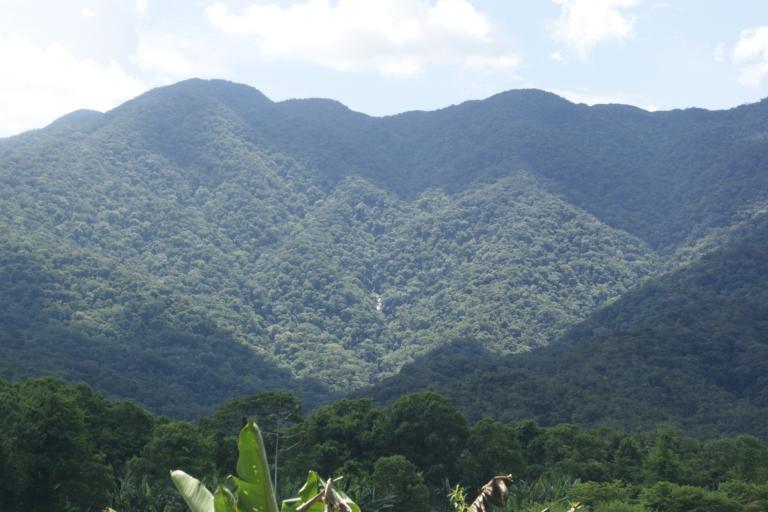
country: BR
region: Sao Paulo
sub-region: Mongagua
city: Mongagua
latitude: -24.0269
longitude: -46.7061
